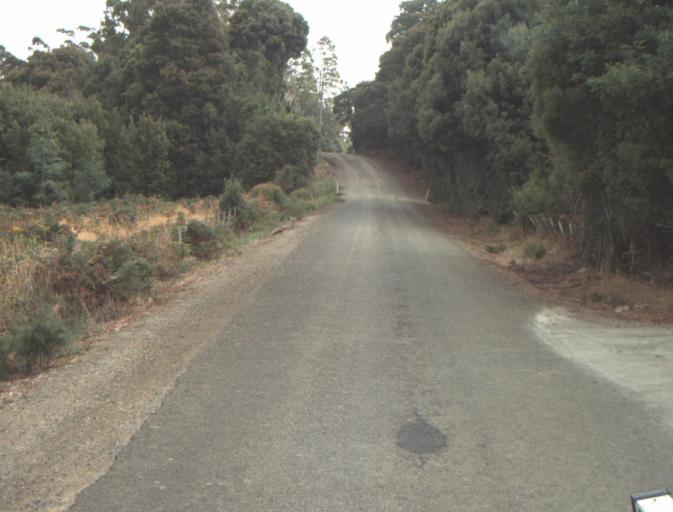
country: AU
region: Tasmania
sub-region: Launceston
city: Mayfield
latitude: -41.2788
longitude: 147.1917
